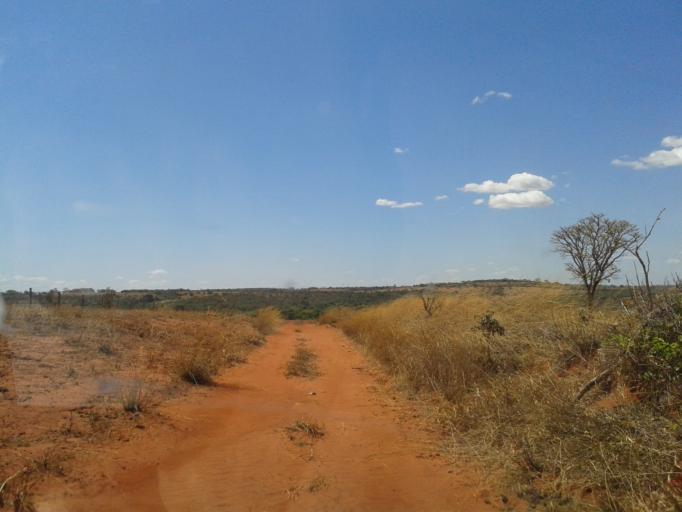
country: BR
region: Minas Gerais
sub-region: Monte Alegre De Minas
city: Monte Alegre de Minas
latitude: -18.8028
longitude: -49.0809
